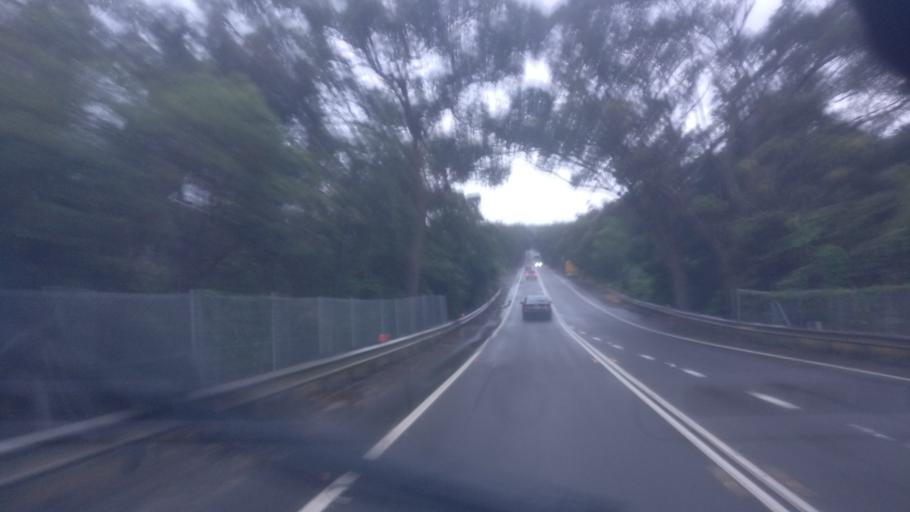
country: AU
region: New South Wales
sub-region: Warringah
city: Allambie Heights
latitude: -33.7438
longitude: 151.2368
